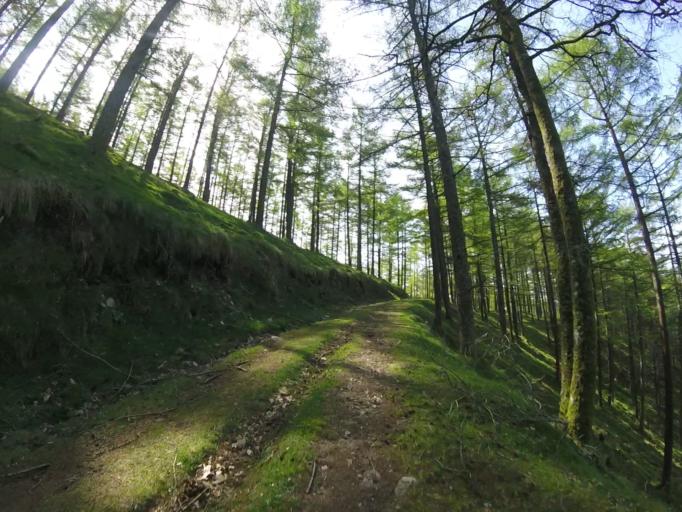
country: ES
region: Navarre
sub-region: Provincia de Navarra
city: Arano
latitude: 43.2562
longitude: -1.8319
